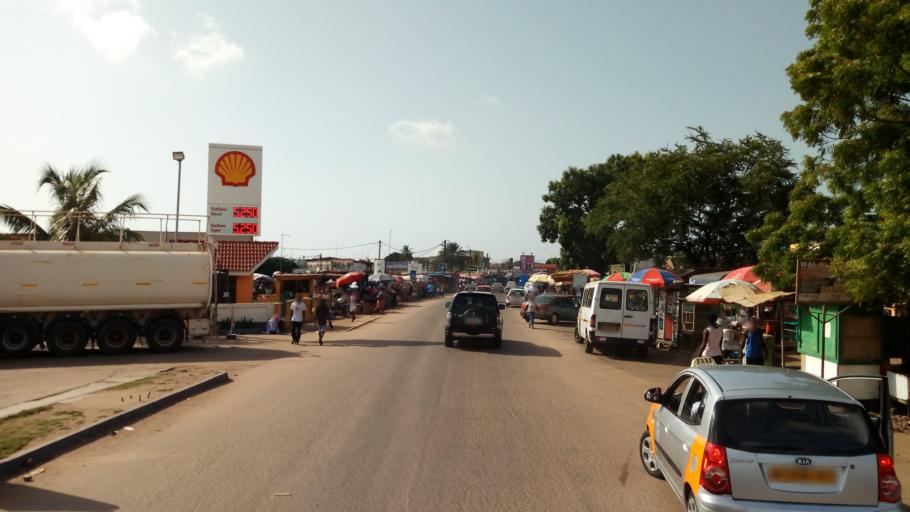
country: GH
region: Greater Accra
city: Tema
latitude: 5.6463
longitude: -0.0017
